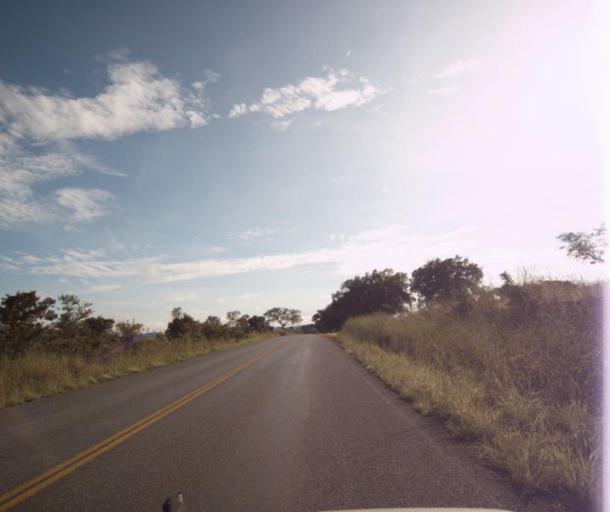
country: BR
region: Goias
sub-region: Pirenopolis
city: Pirenopolis
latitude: -15.5754
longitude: -48.6246
